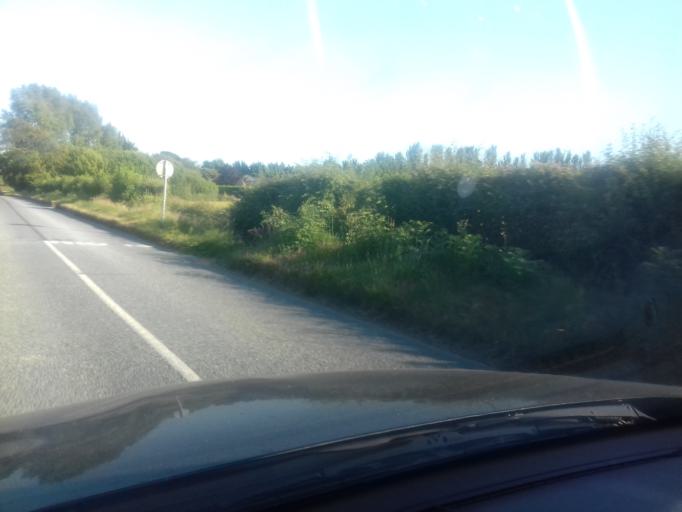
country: IE
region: Leinster
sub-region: An Mhi
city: Ashbourne
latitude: 53.4491
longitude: -6.3934
